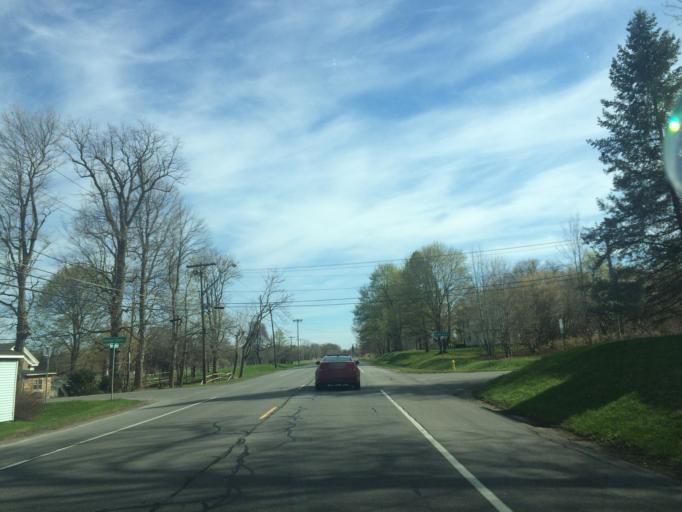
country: US
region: New York
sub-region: Monroe County
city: Webster
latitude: 43.1676
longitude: -77.4312
